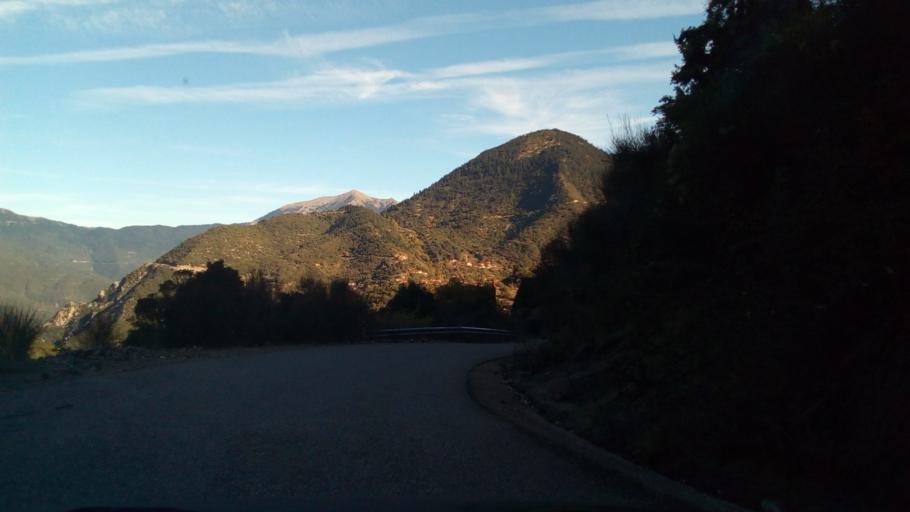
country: GR
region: West Greece
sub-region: Nomos Aitolias kai Akarnanias
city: Nafpaktos
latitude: 38.5511
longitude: 21.8518
